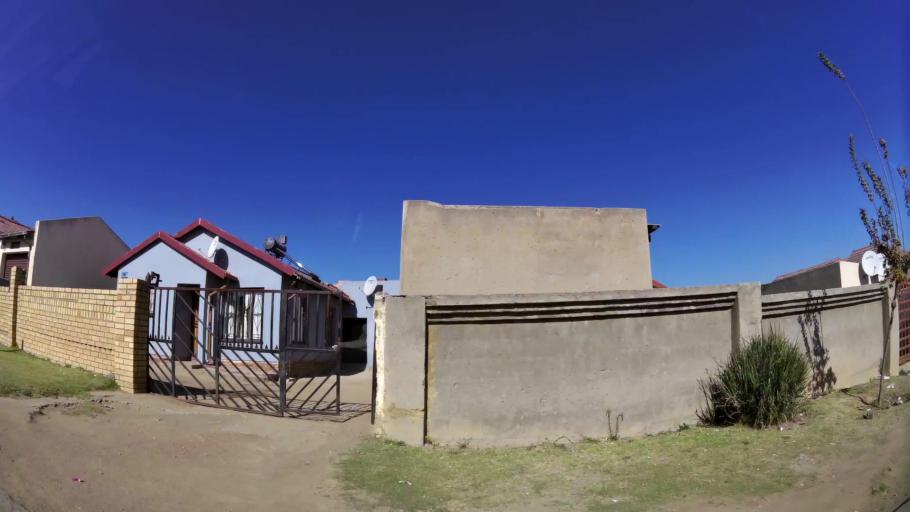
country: ZA
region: Gauteng
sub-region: Ekurhuleni Metropolitan Municipality
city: Tembisa
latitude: -26.0363
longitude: 28.1956
